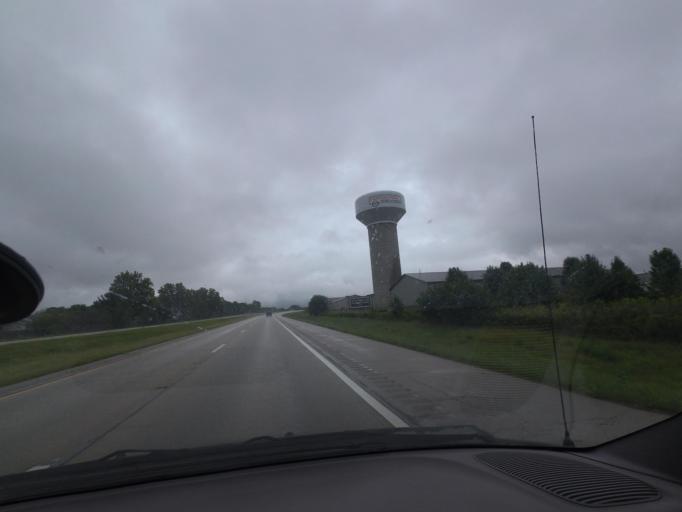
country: US
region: Illinois
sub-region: Champaign County
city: Champaign
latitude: 40.1198
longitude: -88.2949
